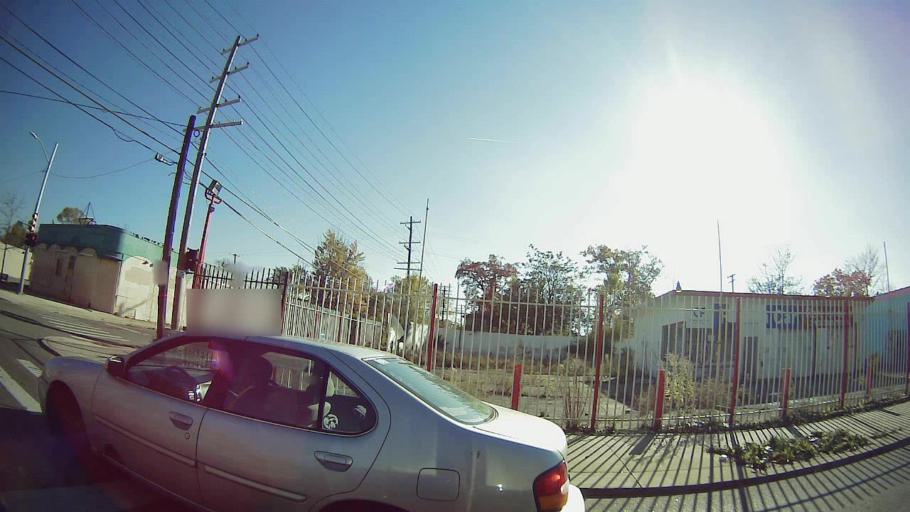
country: US
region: Michigan
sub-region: Wayne County
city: Highland Park
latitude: 42.4321
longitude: -83.1075
